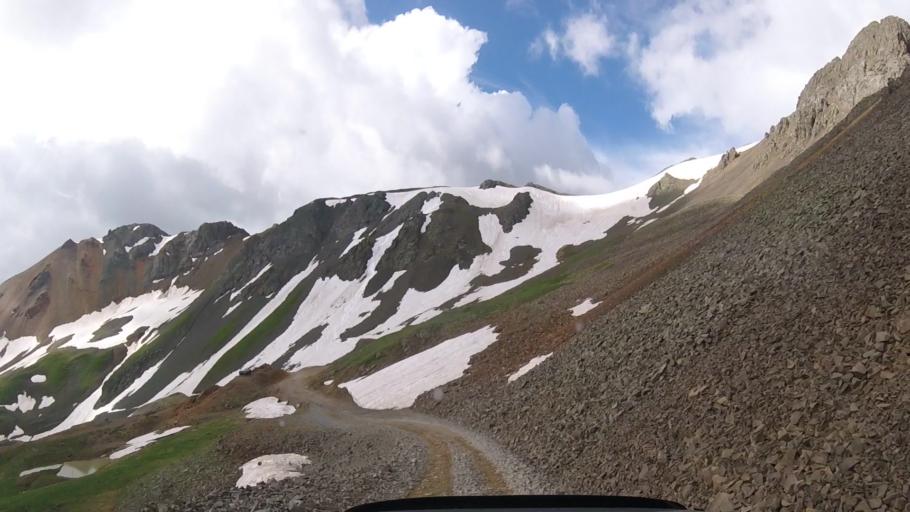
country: US
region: Colorado
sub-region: San Juan County
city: Silverton
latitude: 37.9157
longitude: -107.6179
